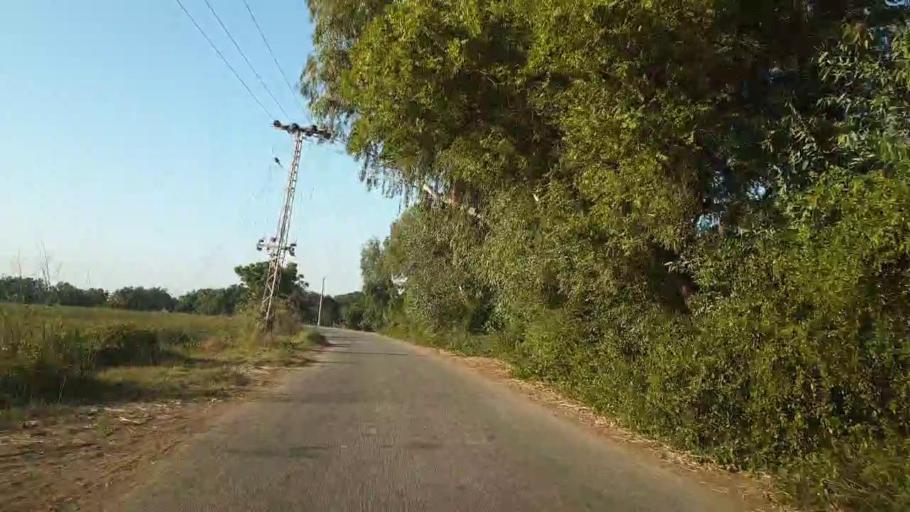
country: PK
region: Sindh
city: Mirpur Khas
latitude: 25.6558
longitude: 69.0968
